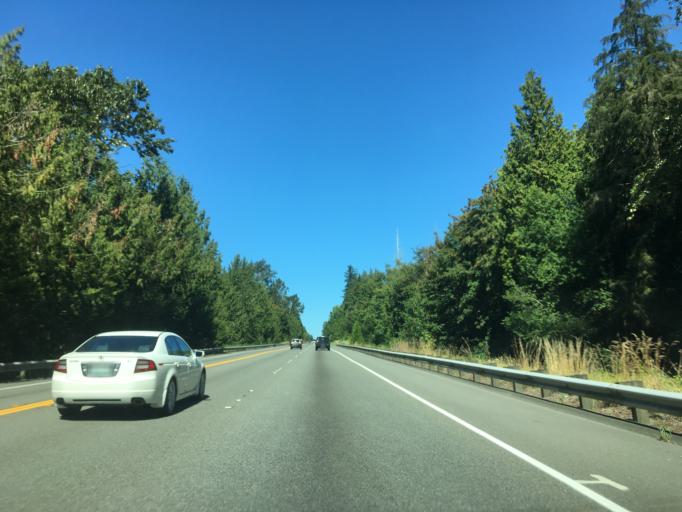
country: US
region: Washington
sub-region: Snohomish County
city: West Lake Stevens
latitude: 47.9900
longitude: -122.1288
